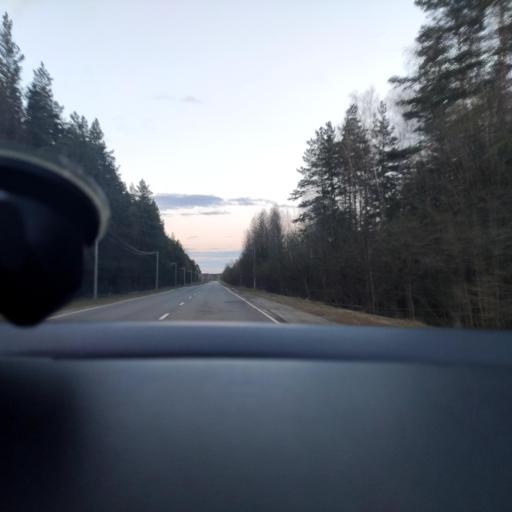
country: RU
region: Moskovskaya
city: Shaturtorf
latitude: 55.4511
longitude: 39.4424
